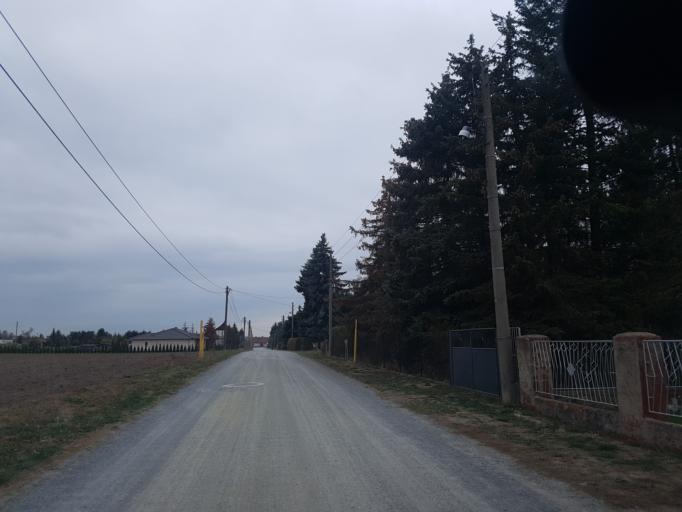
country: DE
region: Brandenburg
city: Finsterwalde
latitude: 51.6158
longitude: 13.7277
